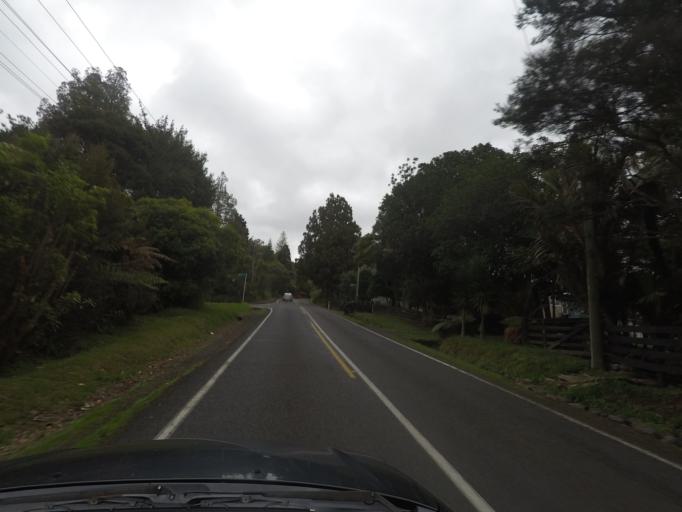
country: NZ
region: Auckland
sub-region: Auckland
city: Titirangi
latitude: -36.9316
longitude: 174.5908
